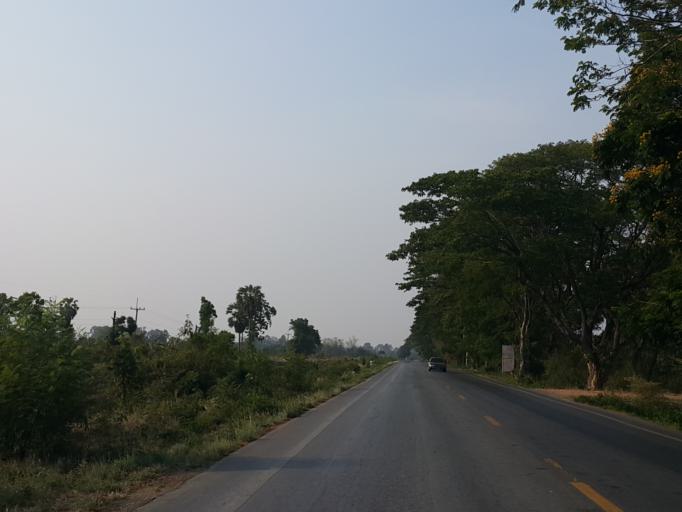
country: TH
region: Chai Nat
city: Sankhaburi
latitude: 15.0257
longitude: 100.1447
